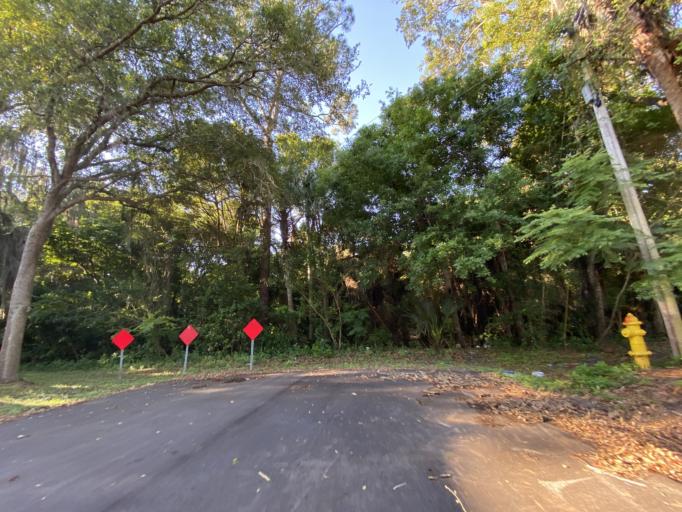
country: US
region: Florida
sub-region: Volusia County
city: Port Orange
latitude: 29.1452
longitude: -80.9950
